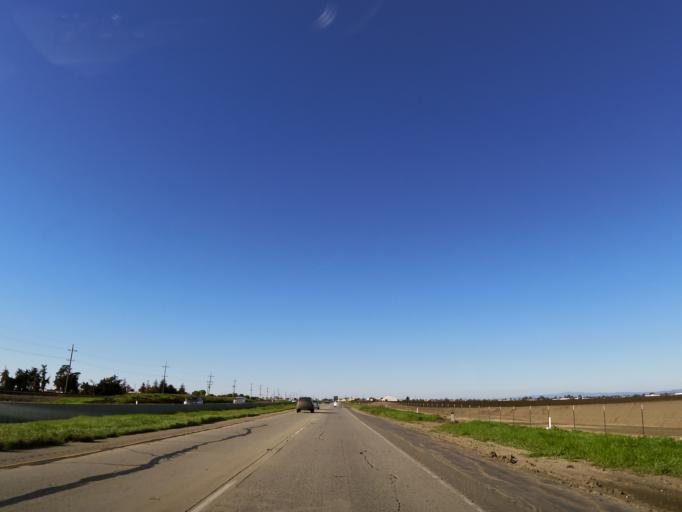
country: US
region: California
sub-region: Monterey County
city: Salinas
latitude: 36.6402
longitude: -121.6044
